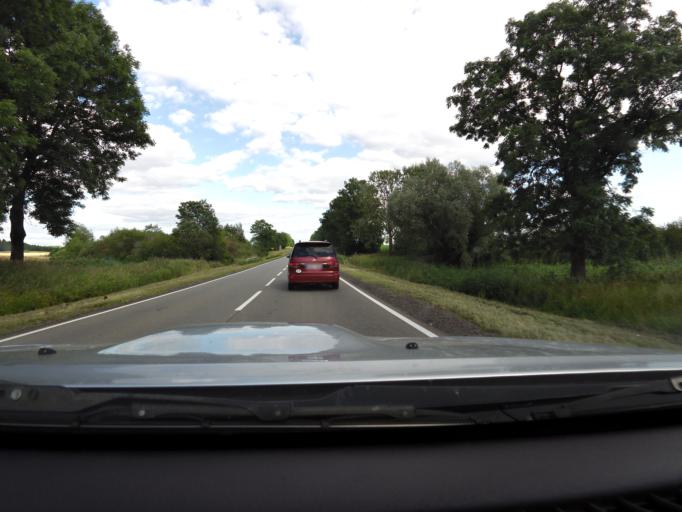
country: PL
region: Podlasie
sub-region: Powiat grajewski
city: Rajgrod
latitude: 53.8611
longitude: 22.7141
